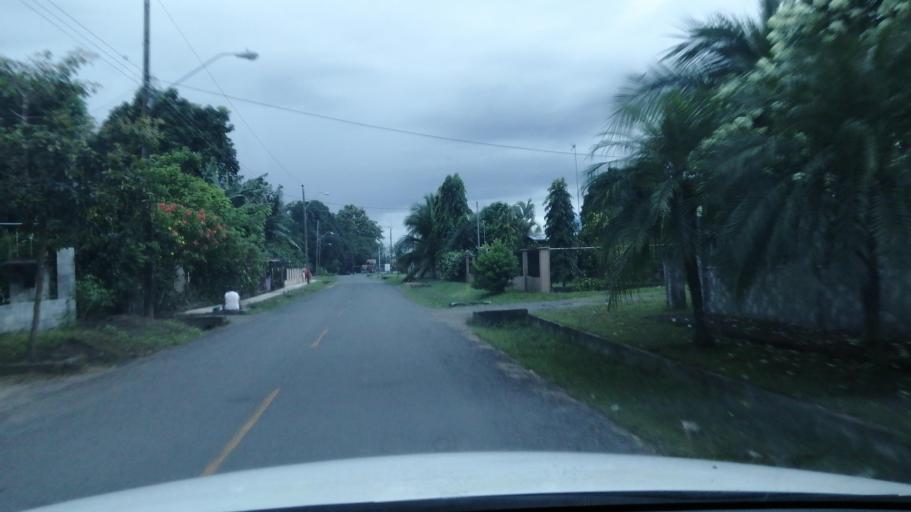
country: PA
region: Chiriqui
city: Alanje
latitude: 8.4114
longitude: -82.5033
